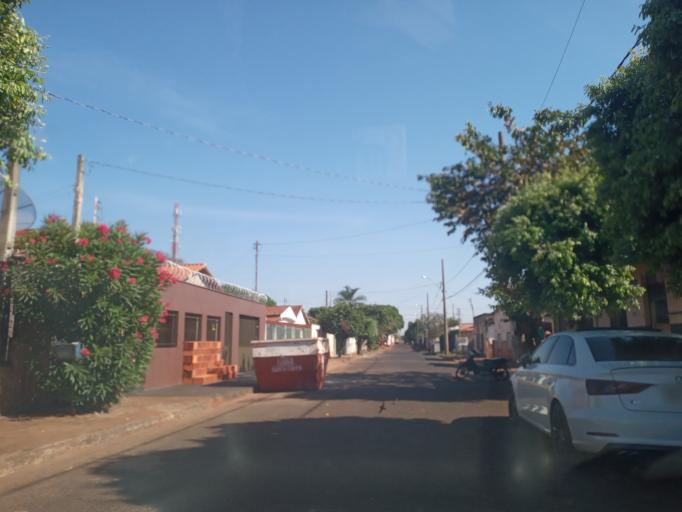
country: BR
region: Minas Gerais
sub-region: Ituiutaba
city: Ituiutaba
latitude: -18.9581
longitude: -49.4550
